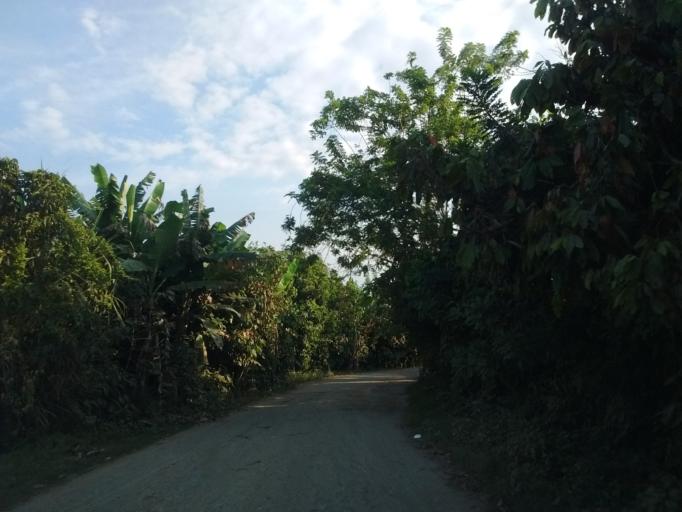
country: CO
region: Cauca
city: Puerto Tejada
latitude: 3.2209
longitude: -76.4468
